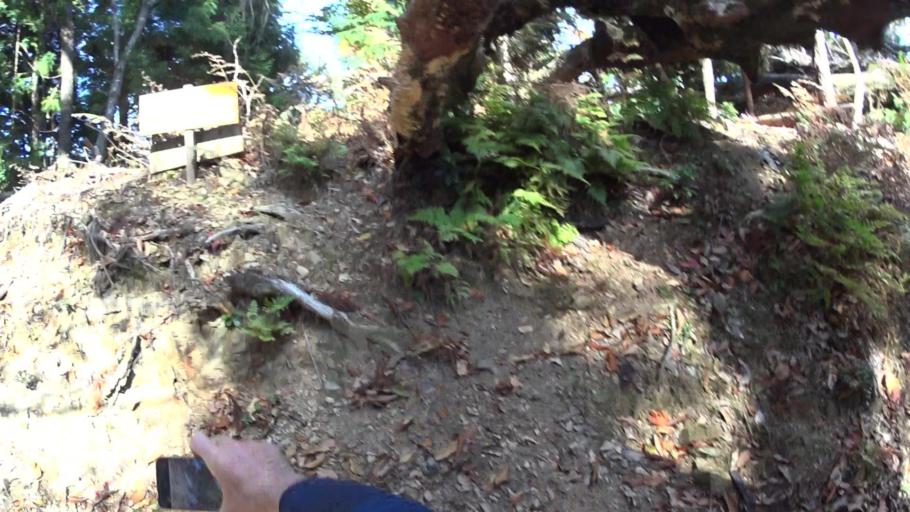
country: JP
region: Kyoto
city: Kameoka
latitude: 35.0475
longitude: 135.6459
